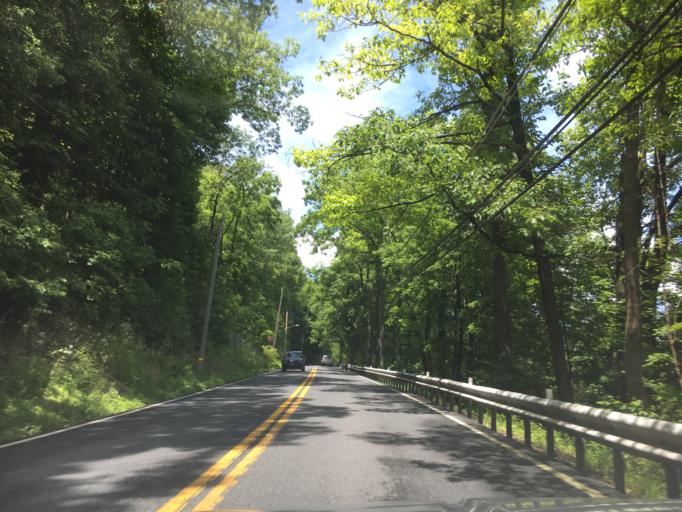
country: US
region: Pennsylvania
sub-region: Lehigh County
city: Cementon
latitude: 40.6943
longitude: -75.5112
